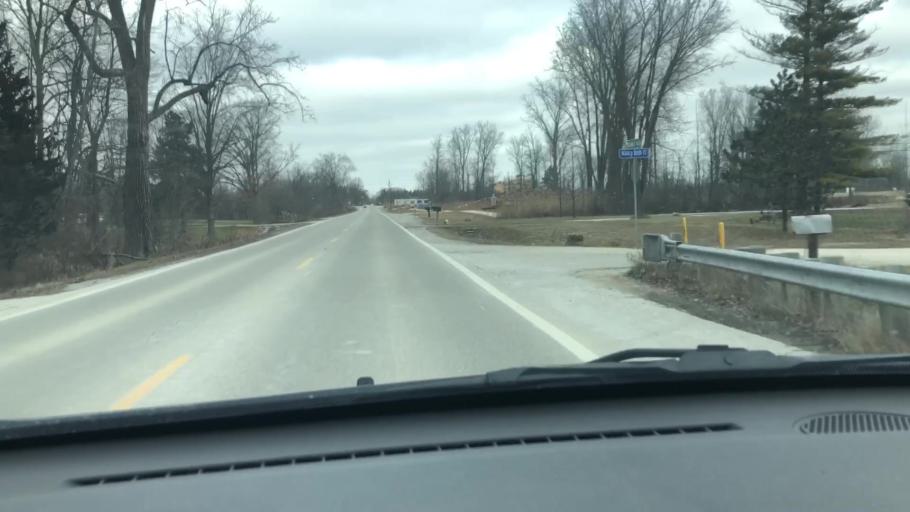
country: US
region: Michigan
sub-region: Macomb County
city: Romeo
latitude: 42.7392
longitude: -83.0173
